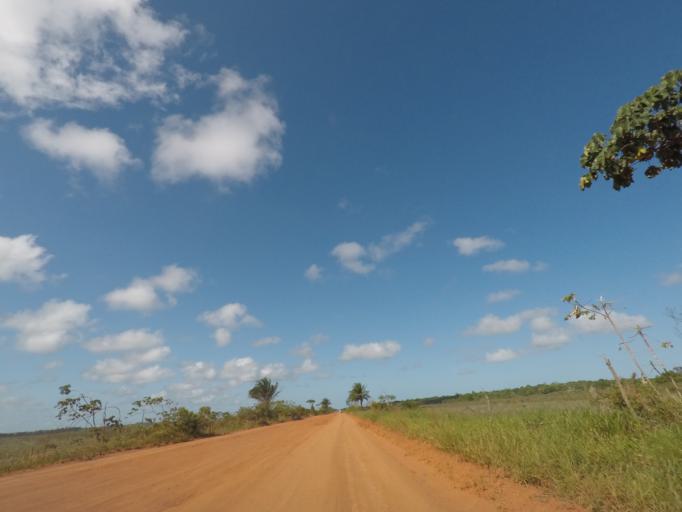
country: BR
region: Bahia
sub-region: Marau
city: Marau
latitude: -14.1721
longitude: -39.0183
